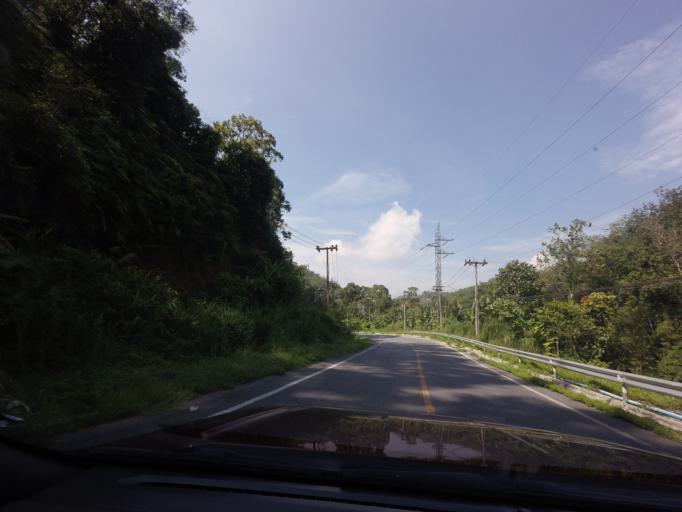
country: TH
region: Yala
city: Betong
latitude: 5.8902
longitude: 101.1455
